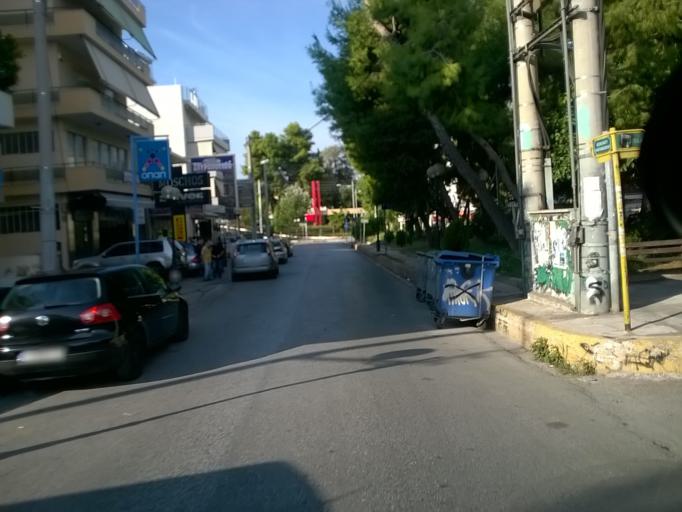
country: GR
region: Attica
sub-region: Nomarchia Athinas
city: Agios Dimitrios
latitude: 37.9400
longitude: 23.7294
